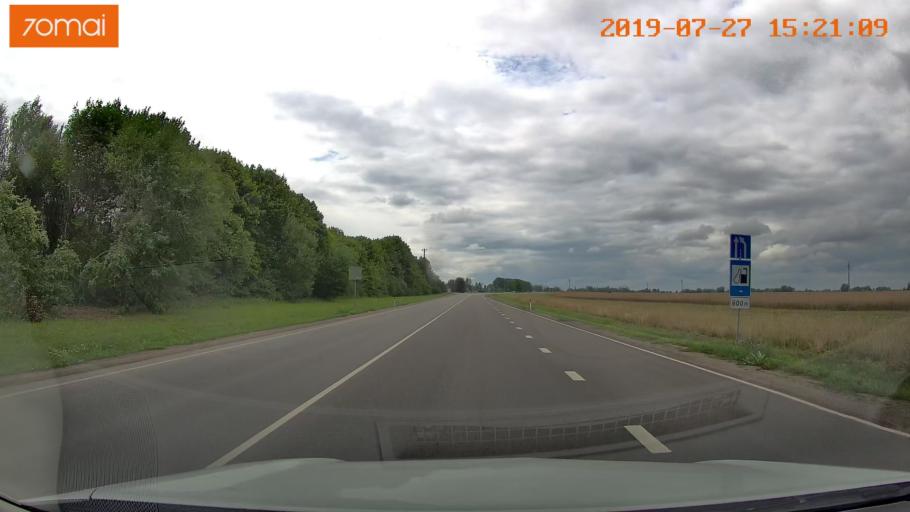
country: LT
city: Kybartai
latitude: 54.6327
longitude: 22.6863
